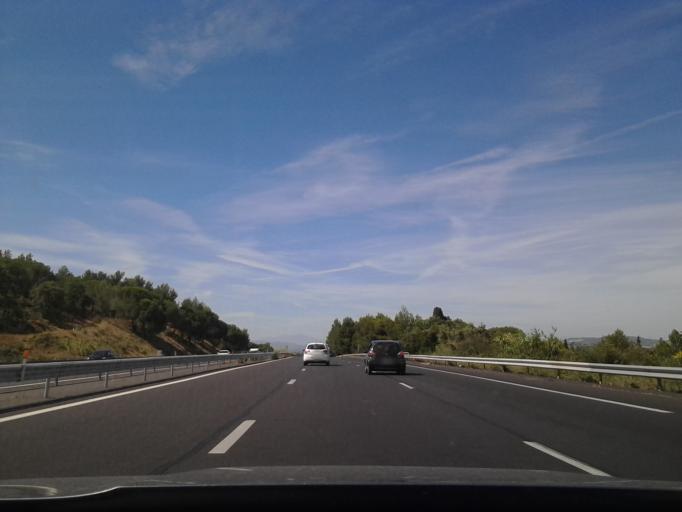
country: FR
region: Languedoc-Roussillon
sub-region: Departement de l'Aude
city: Vinassan
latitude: 43.2054
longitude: 3.0838
